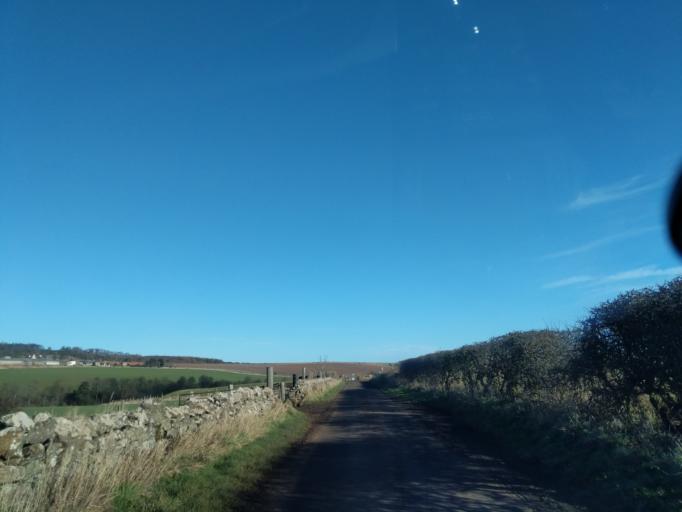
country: GB
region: Scotland
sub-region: East Lothian
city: East Linton
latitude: 55.9707
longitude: -2.6926
